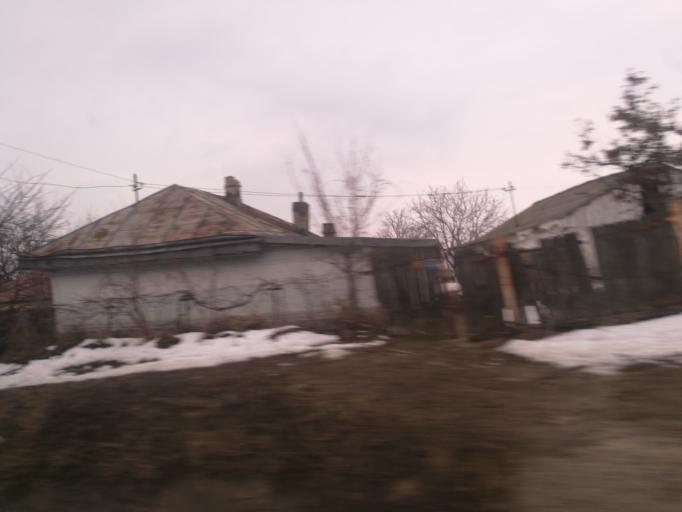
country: RO
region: Iasi
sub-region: Comuna Targu Frumos
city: Targu Frumos
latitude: 47.2047
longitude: 26.9950
